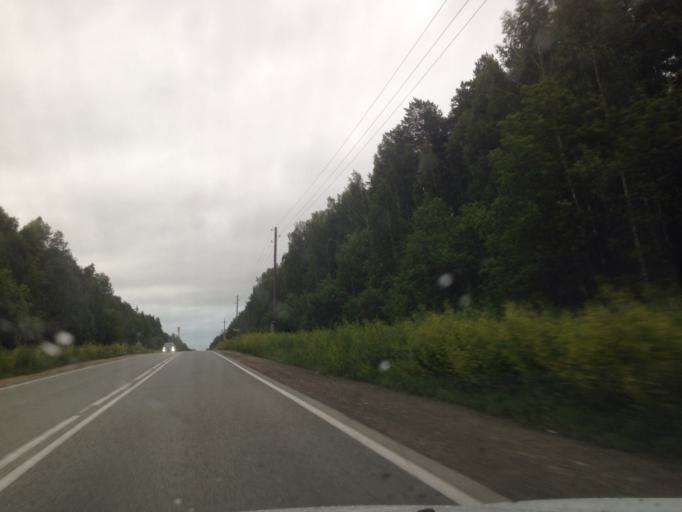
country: RU
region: Sverdlovsk
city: Istok
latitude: 56.8393
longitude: 60.7737
